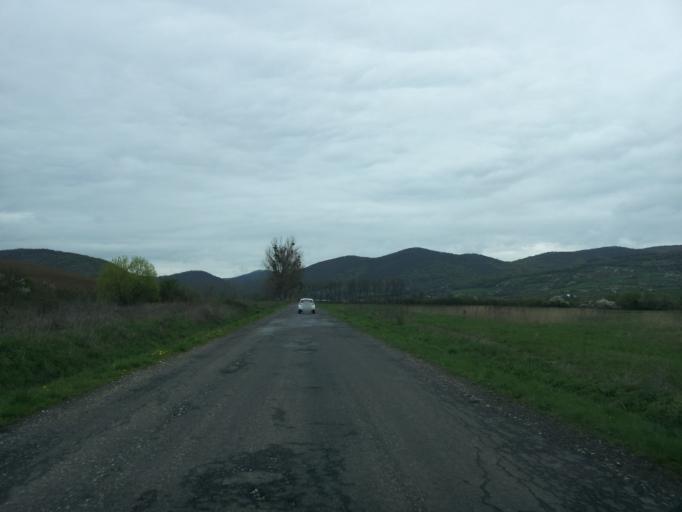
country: HU
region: Borsod-Abauj-Zemplen
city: Szendro
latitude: 48.5051
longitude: 20.6864
